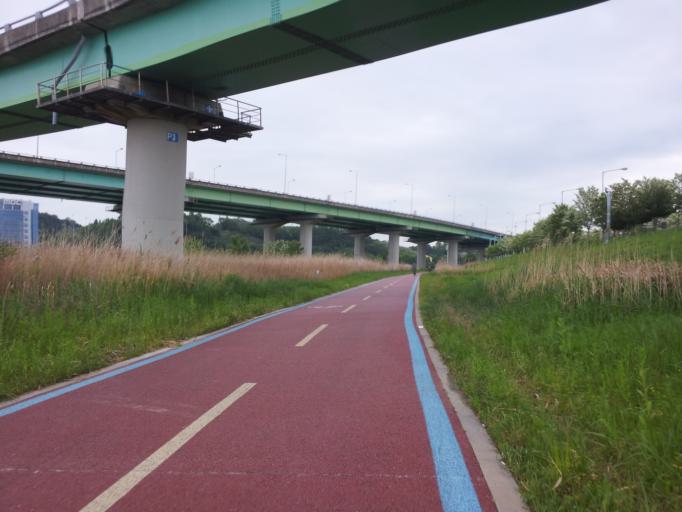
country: KR
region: Daejeon
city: Daejeon
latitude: 36.3711
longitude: 127.3974
